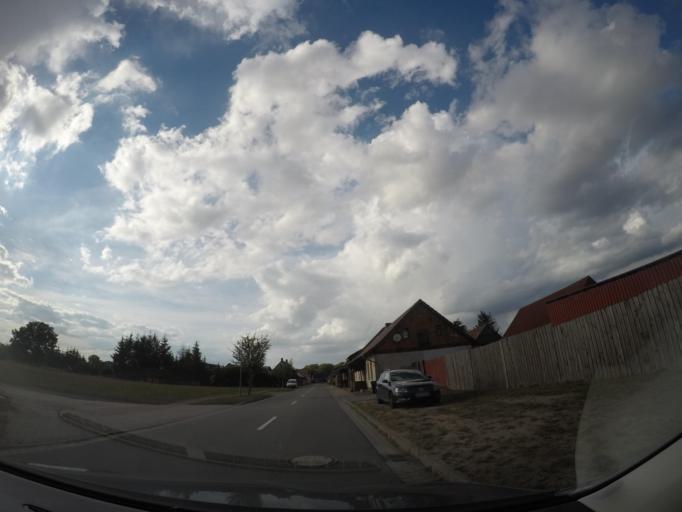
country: DE
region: Saxony-Anhalt
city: Mieste
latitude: 52.4732
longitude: 11.2639
